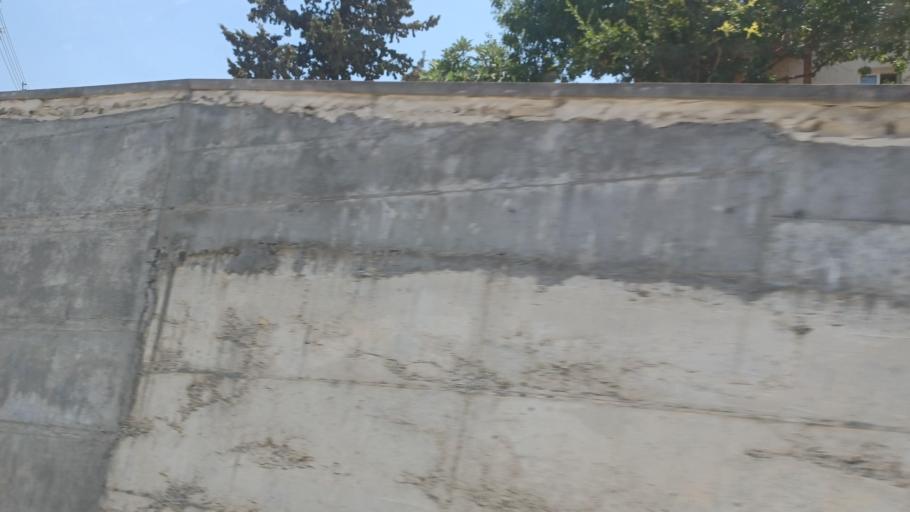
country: CY
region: Pafos
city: Mesogi
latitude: 34.8181
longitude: 32.4563
